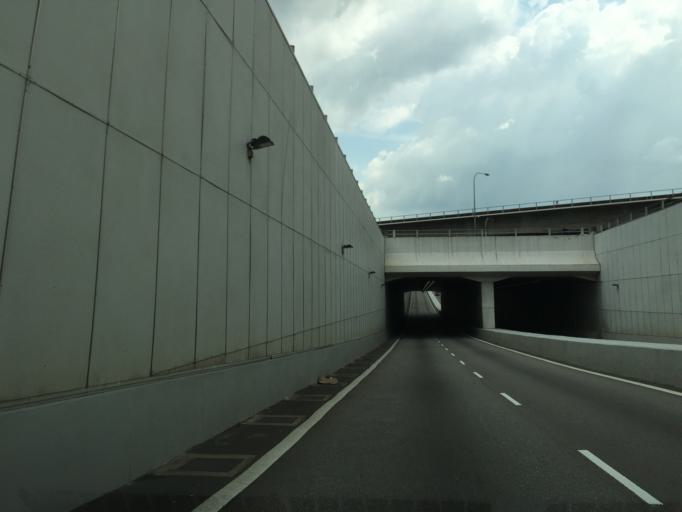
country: SG
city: Singapore
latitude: 1.2992
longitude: 103.8006
